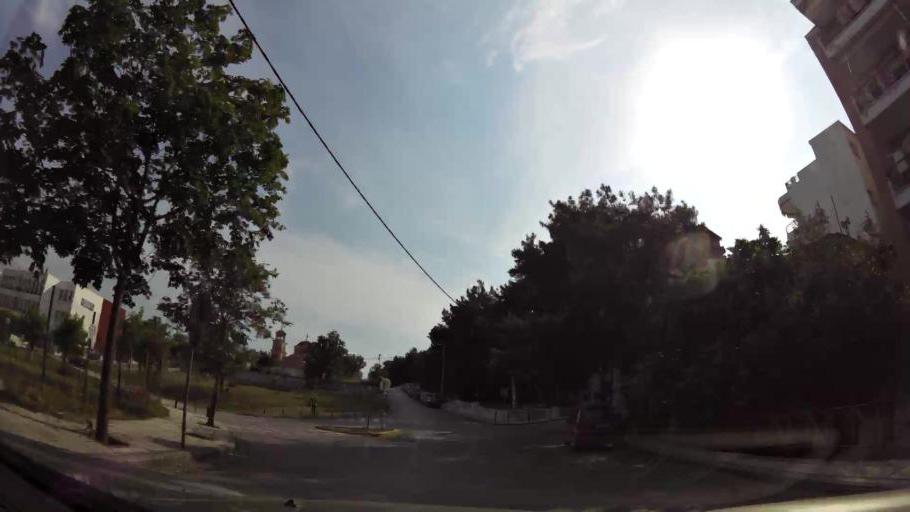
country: GR
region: Central Macedonia
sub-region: Nomos Thessalonikis
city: Sykies
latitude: 40.6535
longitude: 22.9475
